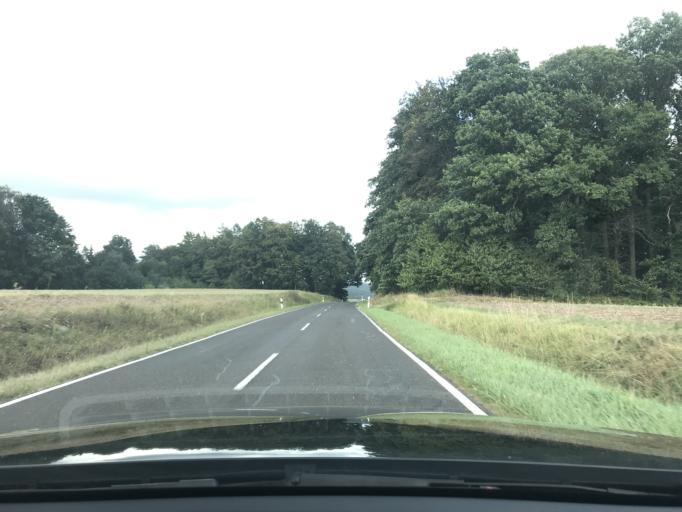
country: DE
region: Bavaria
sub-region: Regierungsbezirk Unterfranken
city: Kirchlauter
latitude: 50.0727
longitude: 10.6802
